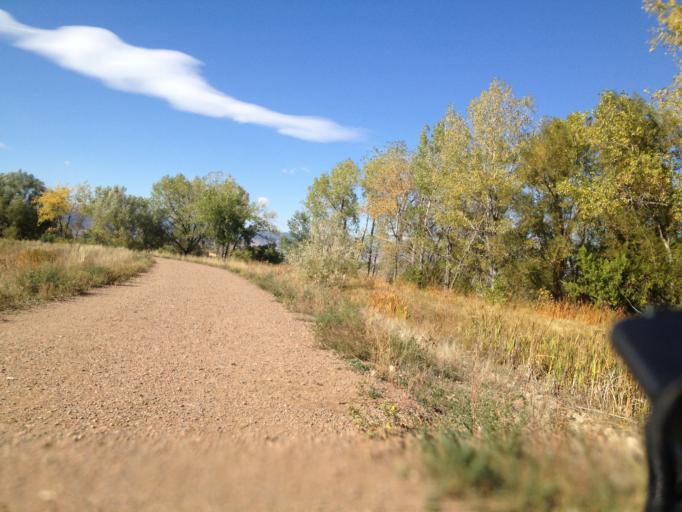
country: US
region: Colorado
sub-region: Boulder County
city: Boulder
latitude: 39.9779
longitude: -105.2255
